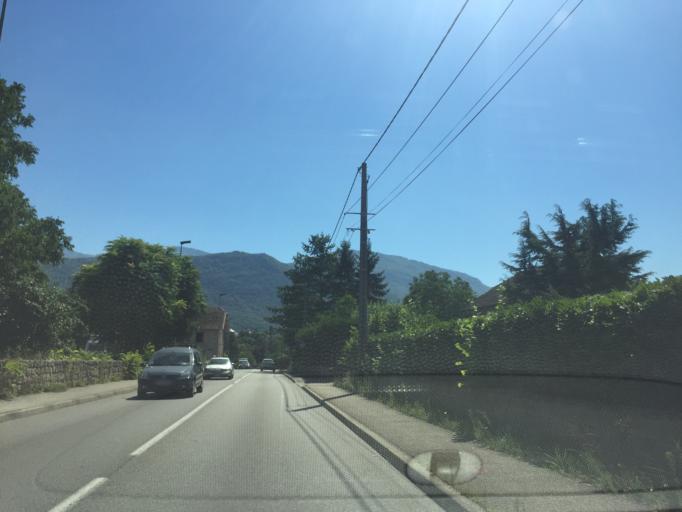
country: FR
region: Rhone-Alpes
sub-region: Departement de la Savoie
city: La Ravoire
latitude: 45.5590
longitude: 5.9544
